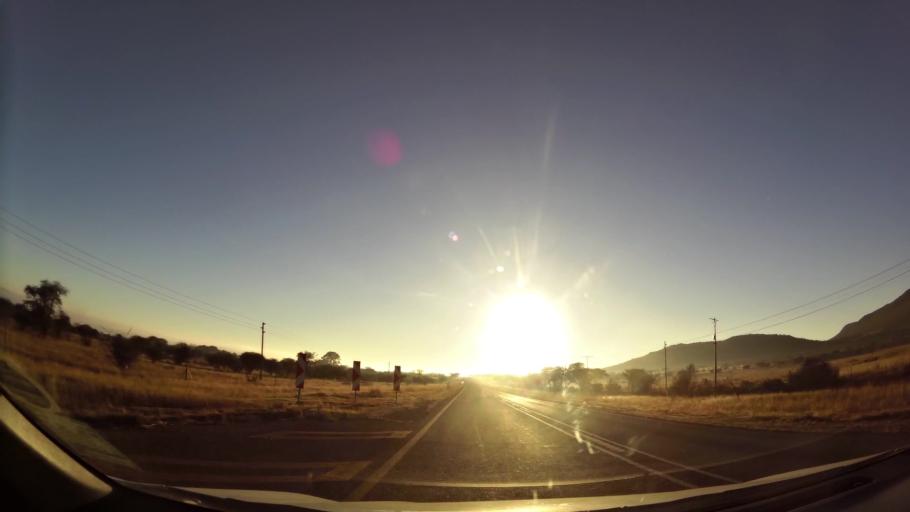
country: ZA
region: Limpopo
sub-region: Capricorn District Municipality
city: Polokwane
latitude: -24.0108
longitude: 29.3259
